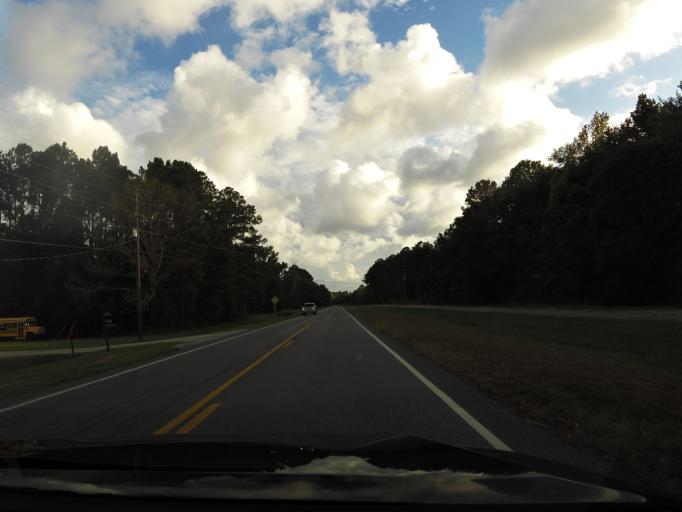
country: US
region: Georgia
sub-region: Liberty County
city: Midway
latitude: 31.7176
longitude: -81.4166
